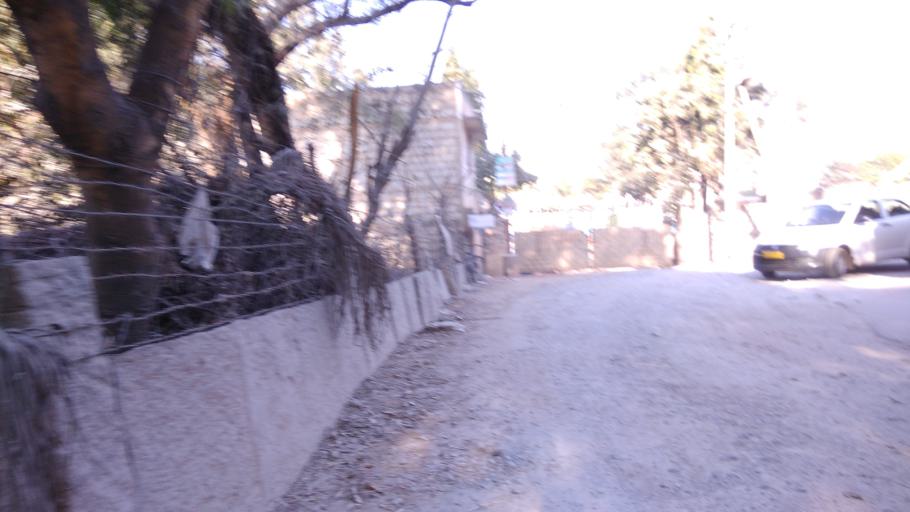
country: IN
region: Karnataka
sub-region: Bangalore Rural
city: Hoskote
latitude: 12.9765
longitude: 77.7397
